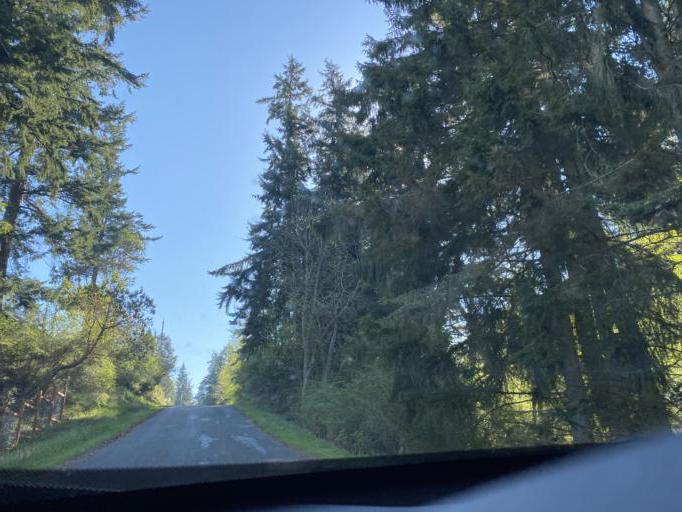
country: US
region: Washington
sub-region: Island County
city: Freeland
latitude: 48.0350
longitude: -122.5967
